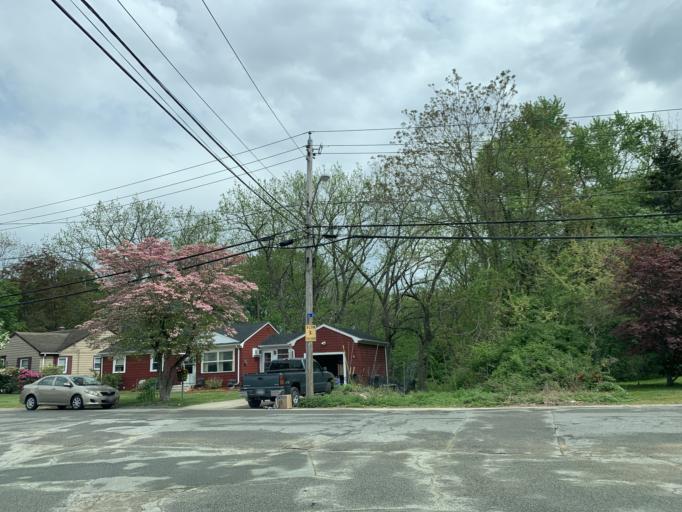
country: US
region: Rhode Island
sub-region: Providence County
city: Johnston
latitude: 41.8014
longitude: -71.4745
